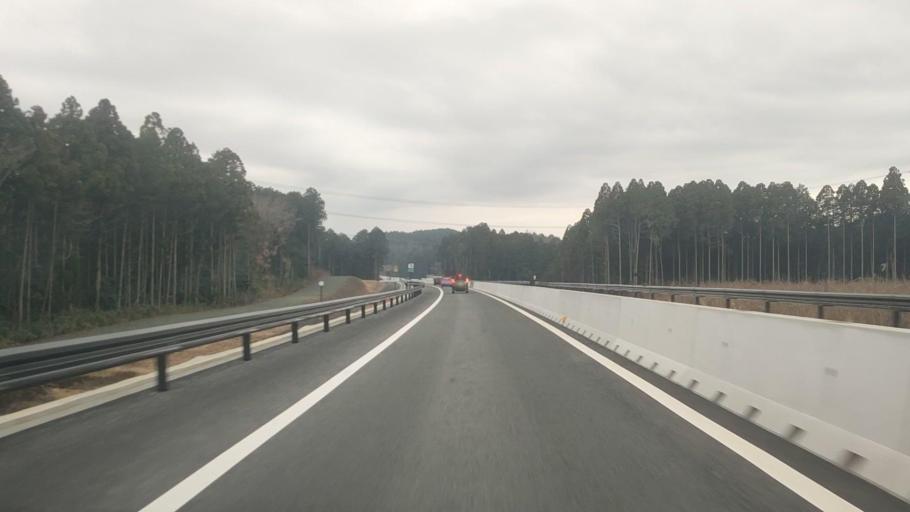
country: JP
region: Kumamoto
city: Ozu
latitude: 32.8996
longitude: 130.9075
